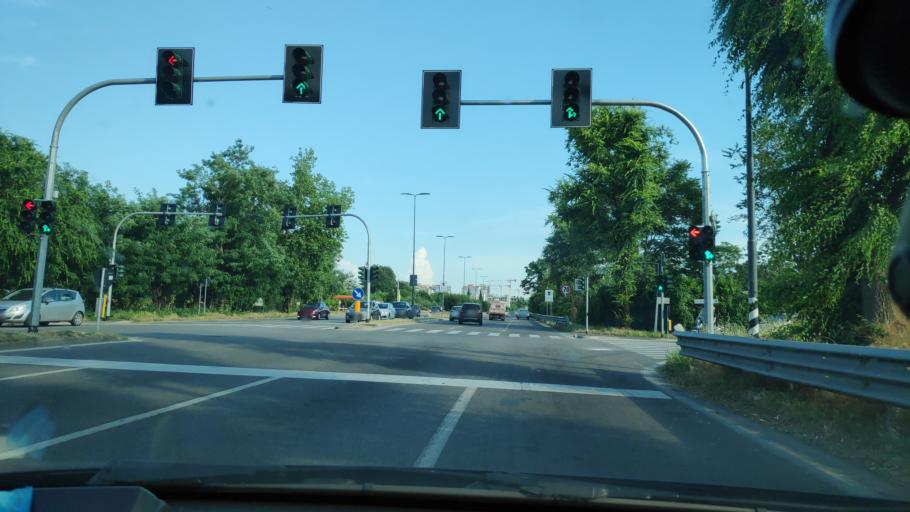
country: IT
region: Lombardy
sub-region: Citta metropolitana di Milano
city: Milano
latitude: 45.4330
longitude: 9.1929
